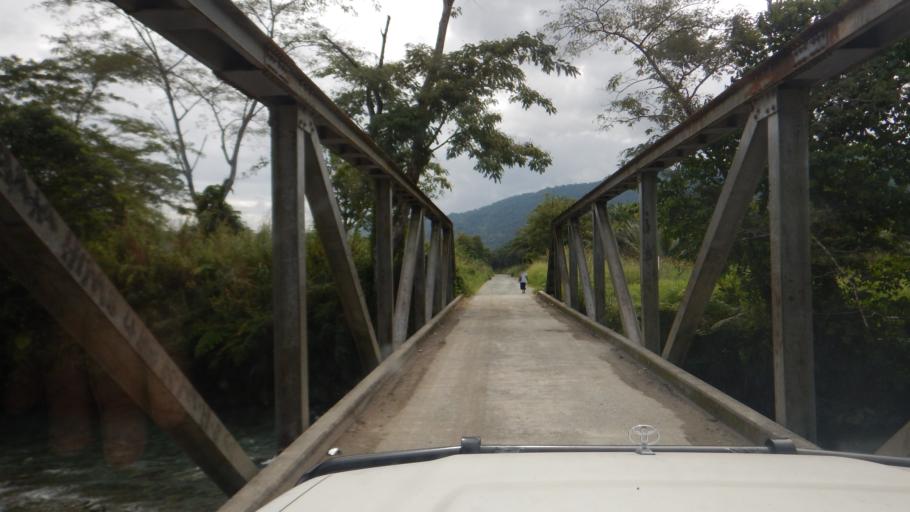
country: PG
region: Northern Province
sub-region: Sohe
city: Kokoda
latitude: -8.9200
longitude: 147.9476
